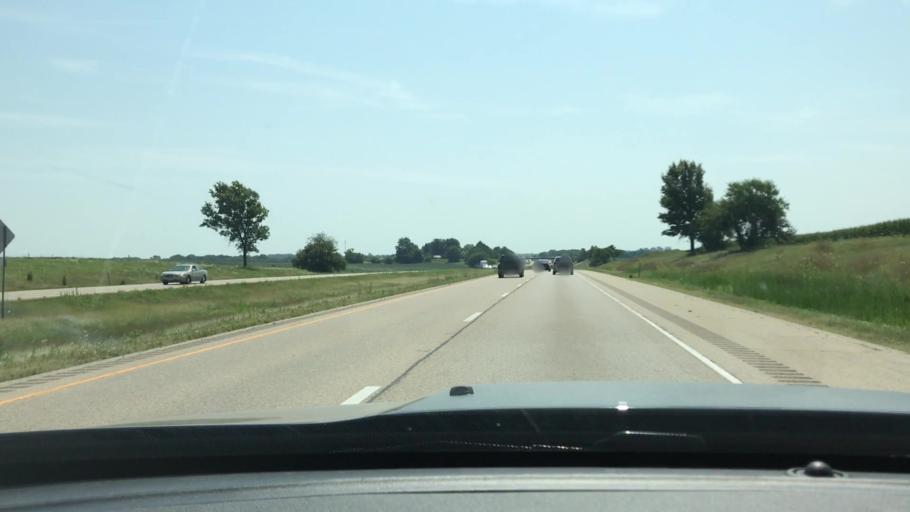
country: US
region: Illinois
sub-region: Bureau County
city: Ladd
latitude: 41.3820
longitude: -89.2672
